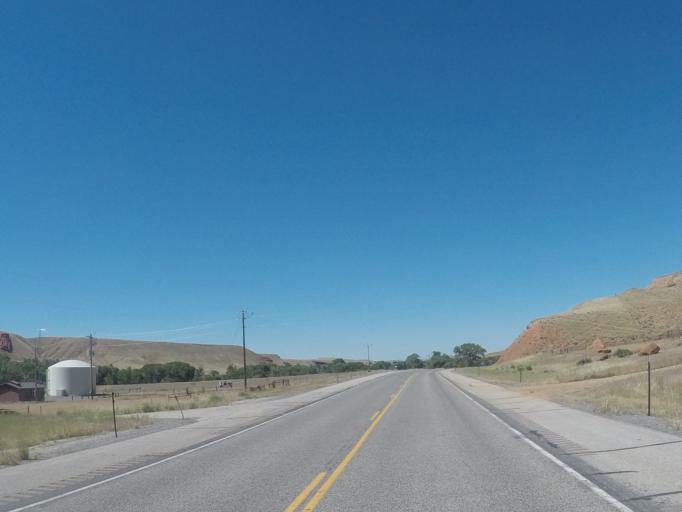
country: US
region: Wyoming
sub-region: Big Horn County
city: Greybull
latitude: 44.5617
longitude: -107.7237
